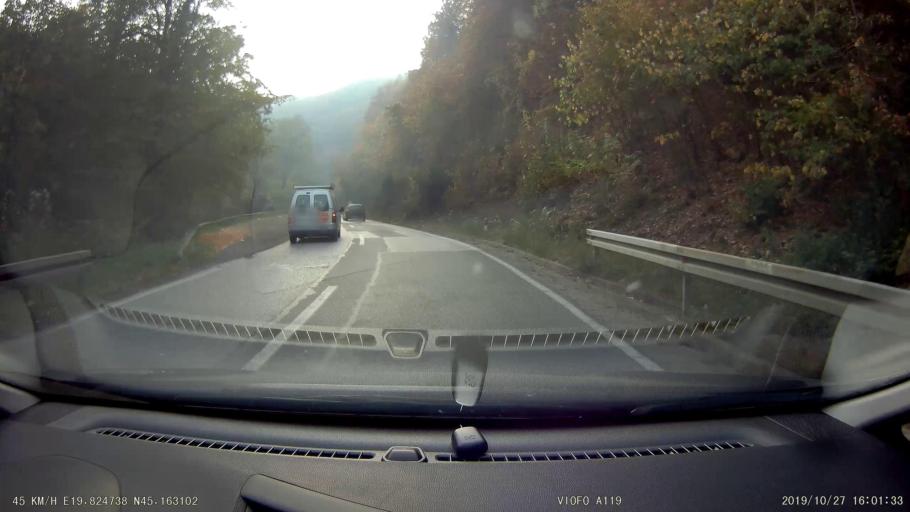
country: RS
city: Vrdnik
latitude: 45.1630
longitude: 19.8245
